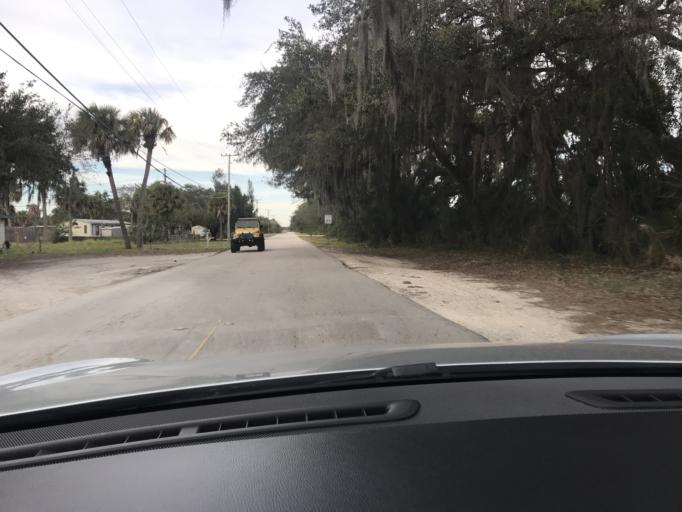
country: US
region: Florida
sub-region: Saint Lucie County
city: Lakewood Park
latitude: 27.4843
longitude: -80.3741
